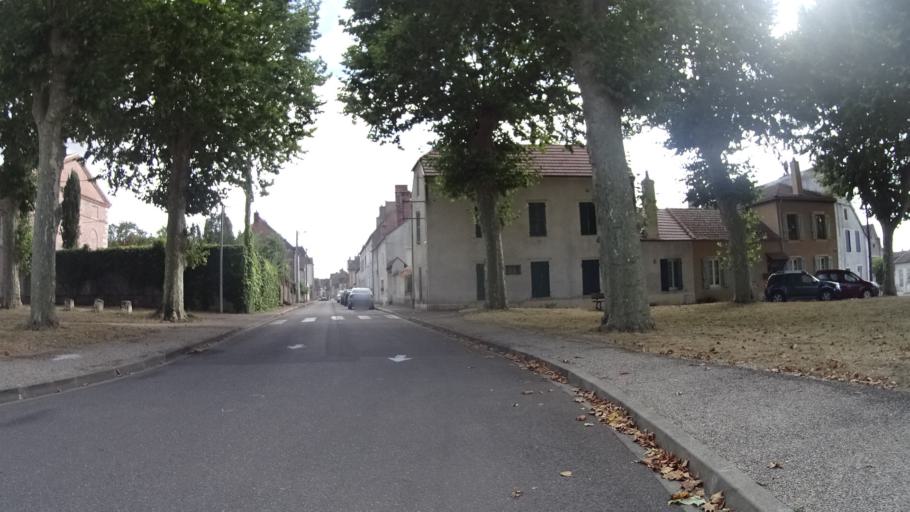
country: FR
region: Bourgogne
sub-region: Departement de la Cote-d'Or
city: Seurre
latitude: 47.0012
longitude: 5.1475
